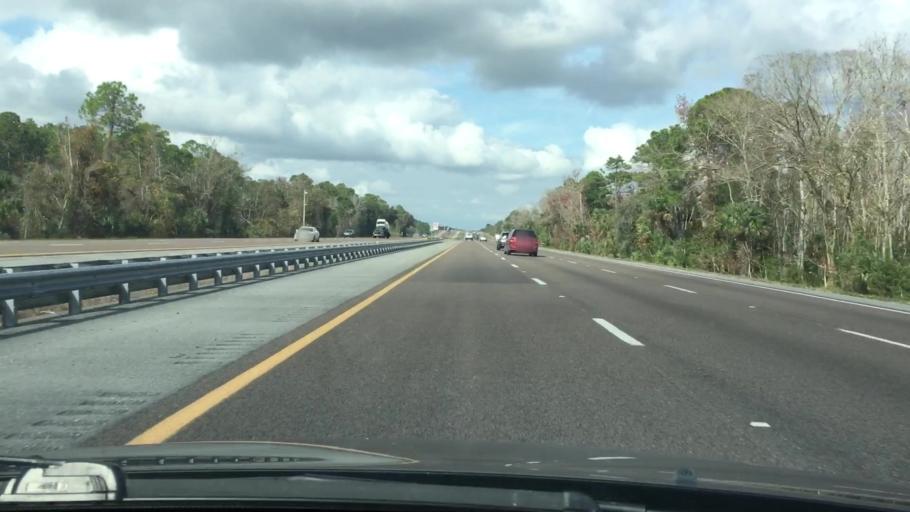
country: US
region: Florida
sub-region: Volusia County
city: Oak Hill
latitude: 28.8231
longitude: -80.9088
